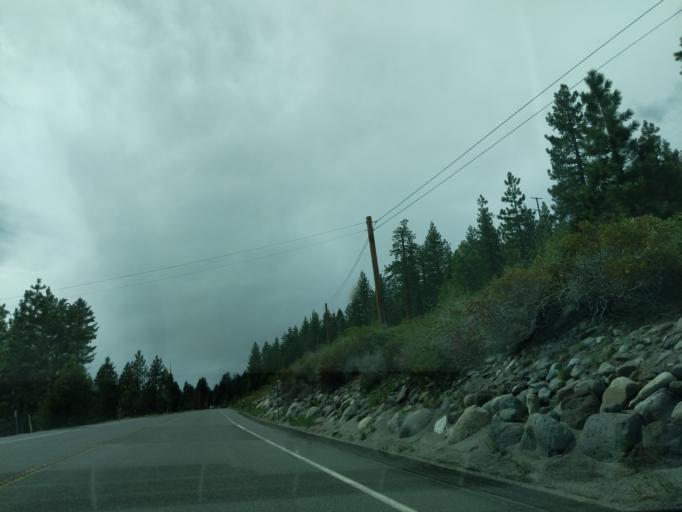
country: US
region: California
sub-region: Placer County
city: Tahoe Vista
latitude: 39.2581
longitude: -120.0556
